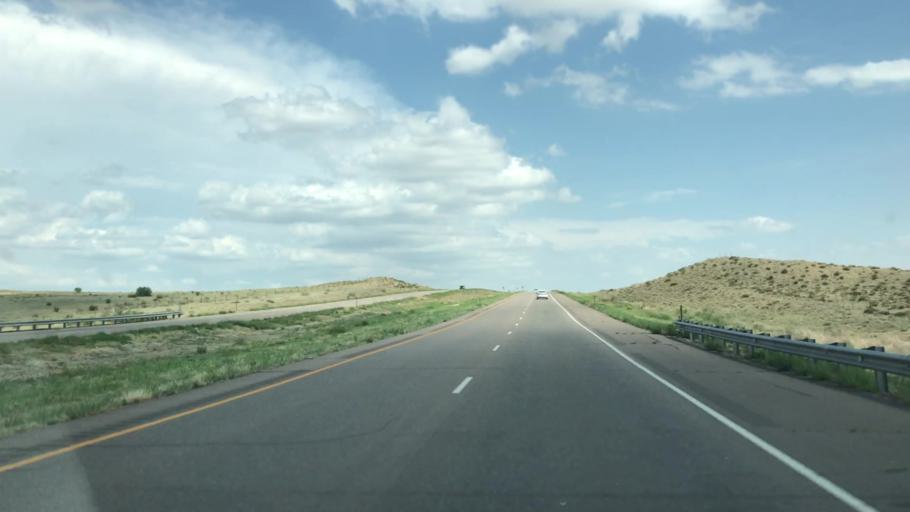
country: US
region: Colorado
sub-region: Fremont County
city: Florence
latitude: 38.4426
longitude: -105.1349
